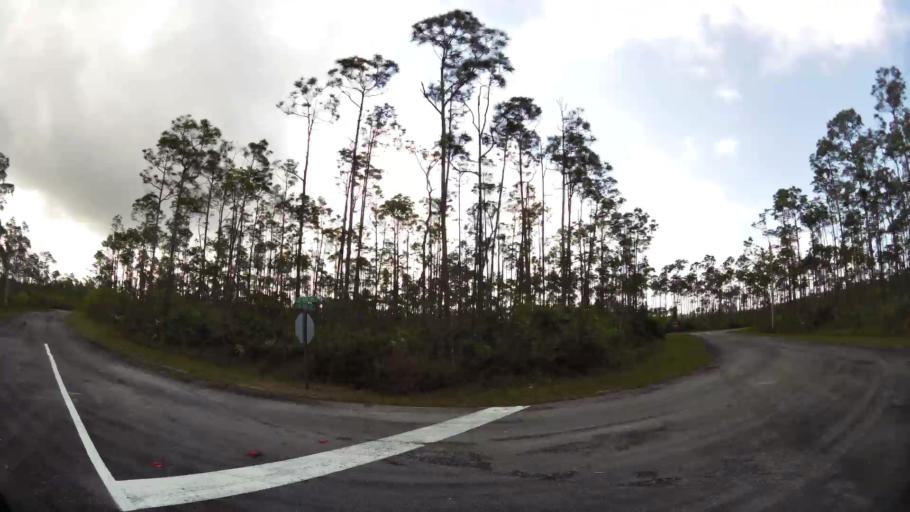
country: BS
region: Freeport
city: Lucaya
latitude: 26.5871
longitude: -78.5524
